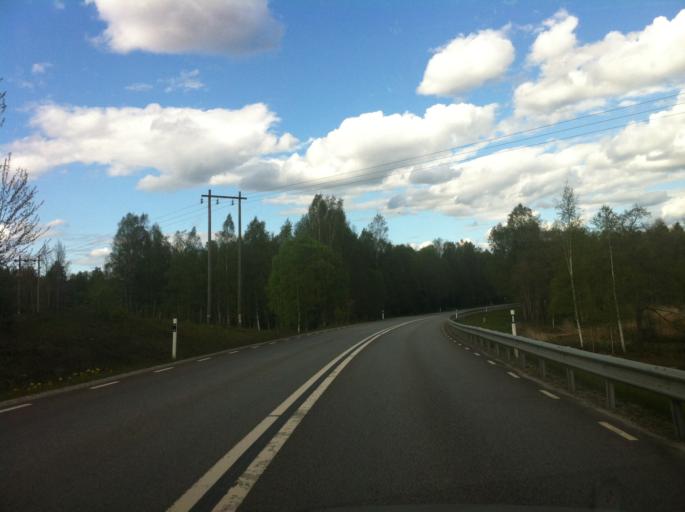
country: SE
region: Vaermland
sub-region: Filipstads Kommun
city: Filipstad
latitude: 59.7397
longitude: 14.2297
